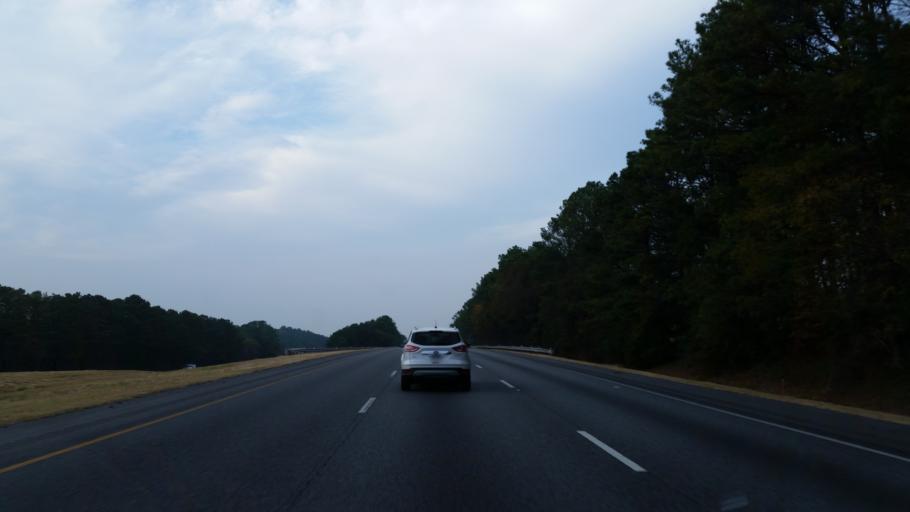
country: US
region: Georgia
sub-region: Bartow County
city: Adairsville
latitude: 34.3864
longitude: -84.9174
